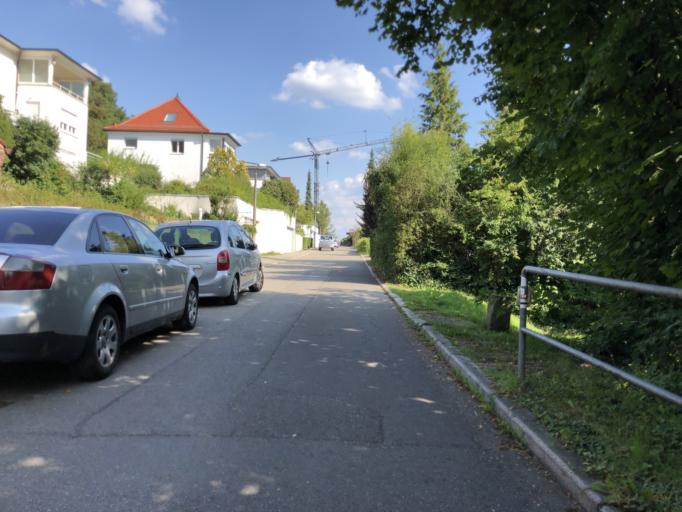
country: DE
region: Baden-Wuerttemberg
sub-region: Regierungsbezirk Stuttgart
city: Sindelfingen
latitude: 48.7120
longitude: 9.0057
